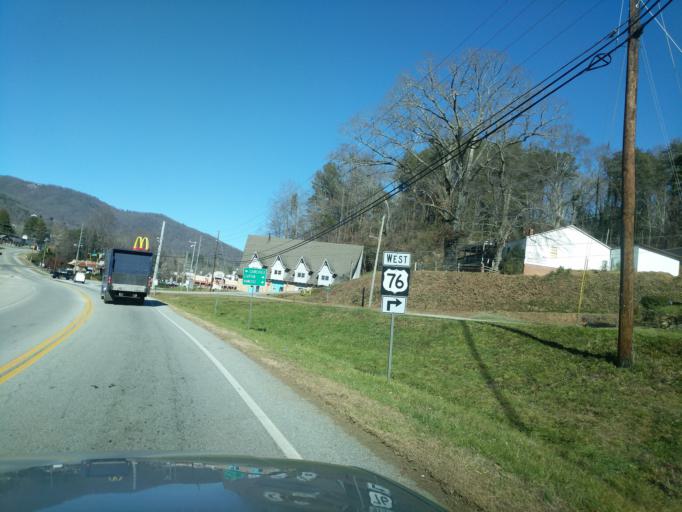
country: US
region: Georgia
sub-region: Rabun County
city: Clayton
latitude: 34.8730
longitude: -83.3981
